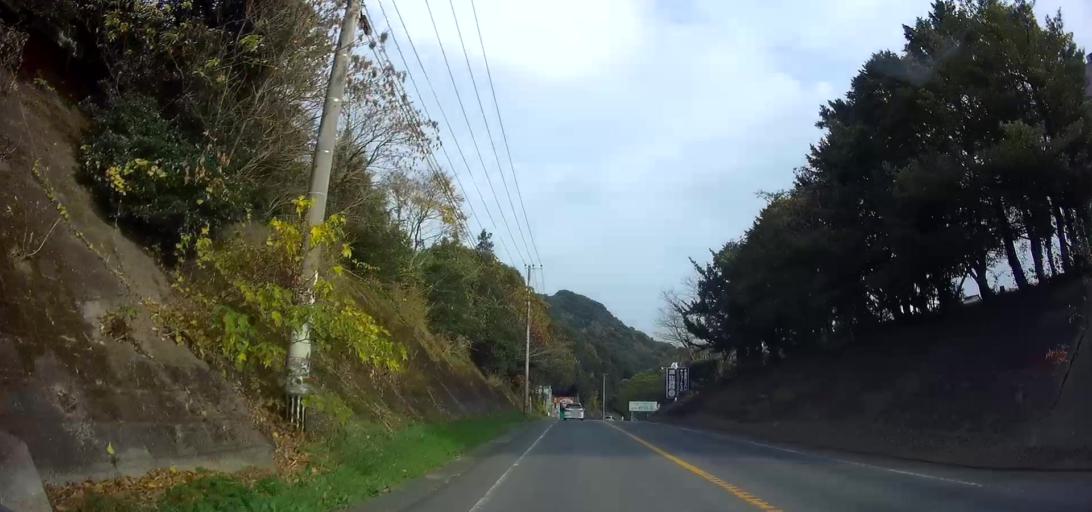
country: JP
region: Nagasaki
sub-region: Isahaya-shi
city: Isahaya
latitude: 32.7969
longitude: 130.1239
